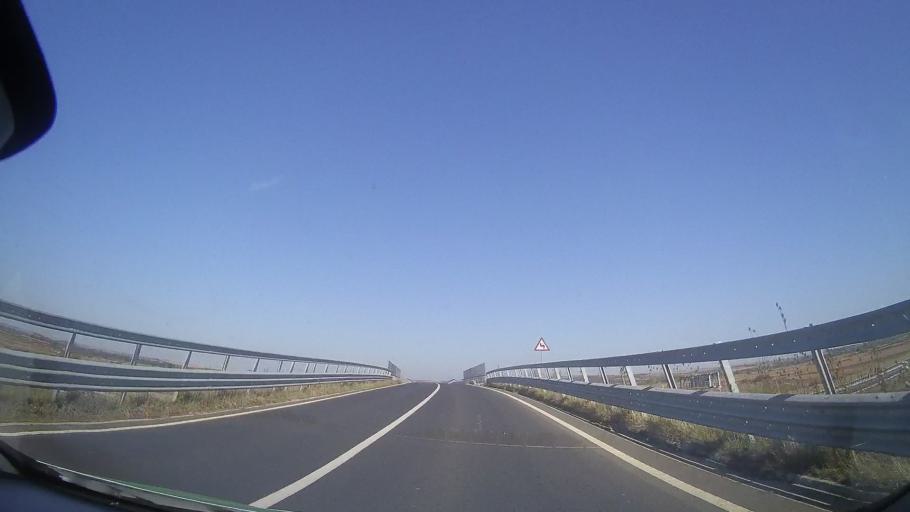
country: RO
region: Timis
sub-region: Comuna Balint
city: Balint
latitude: 45.7979
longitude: 21.8610
